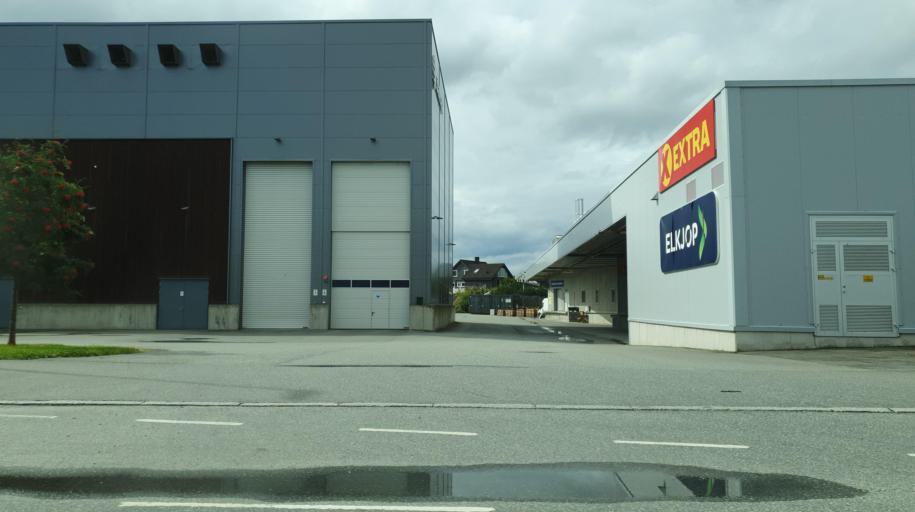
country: NO
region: Nord-Trondelag
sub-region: Stjordal
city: Stjordalshalsen
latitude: 63.4668
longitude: 10.9434
